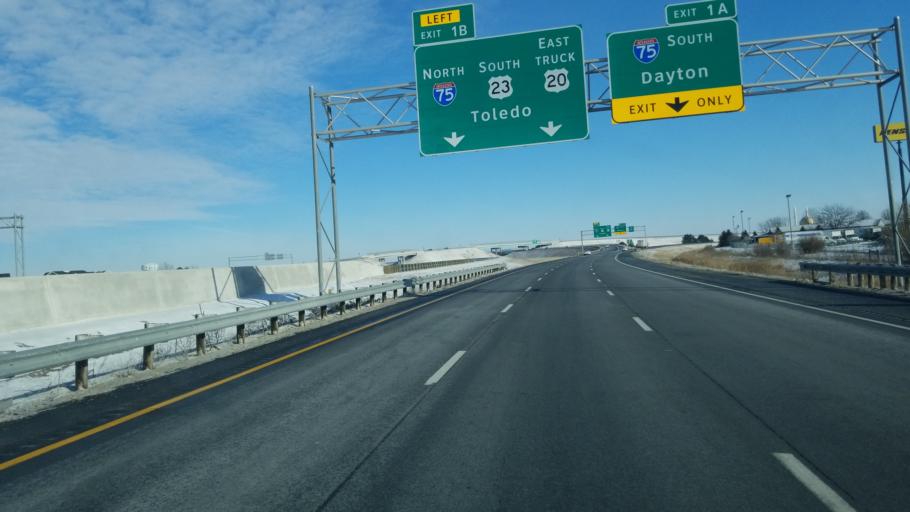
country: US
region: Ohio
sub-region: Wood County
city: Perrysburg
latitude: 41.5323
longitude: -83.6298
